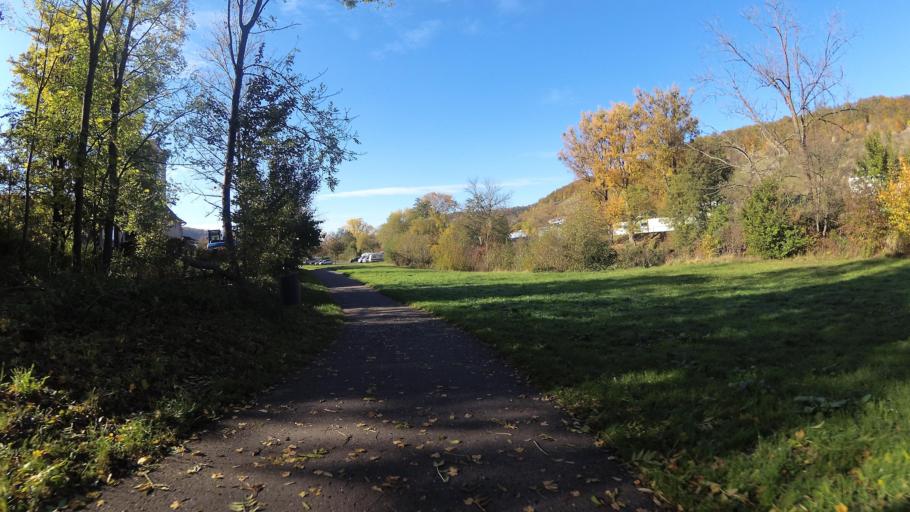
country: DE
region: Baden-Wuerttemberg
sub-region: Regierungsbezirk Stuttgart
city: Forchtenberg
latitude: 49.2903
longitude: 9.5712
